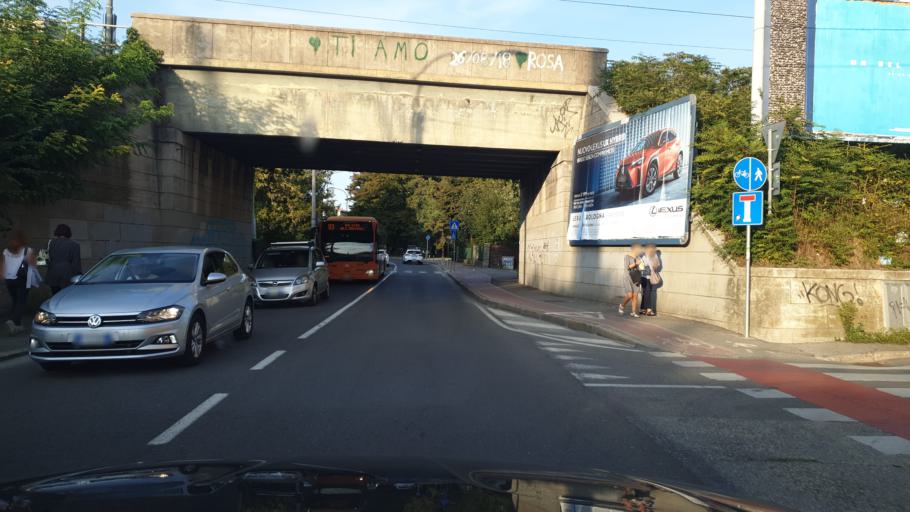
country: IT
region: Emilia-Romagna
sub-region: Provincia di Bologna
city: Bologna
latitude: 44.5069
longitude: 11.3754
